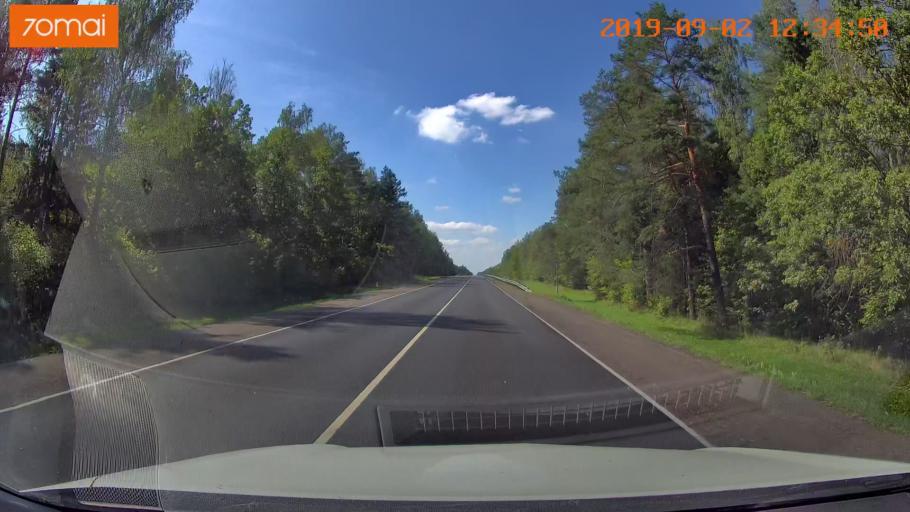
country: RU
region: Smolensk
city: Shumyachi
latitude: 53.8073
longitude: 32.3948
